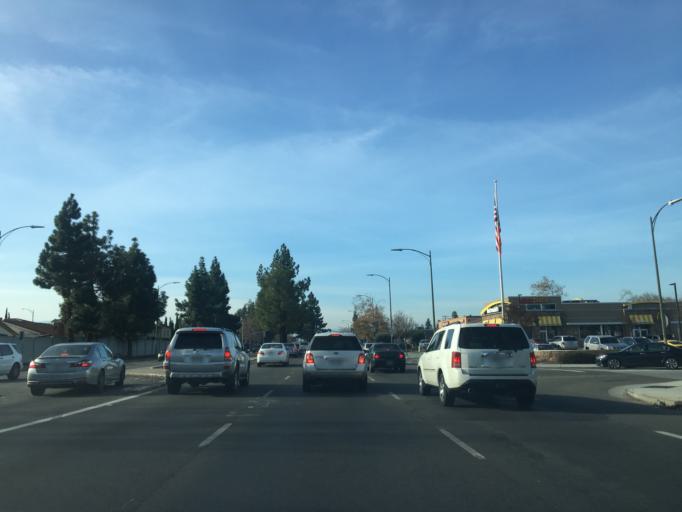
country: US
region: California
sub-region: Santa Clara County
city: Alum Rock
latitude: 37.3251
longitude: -121.8221
